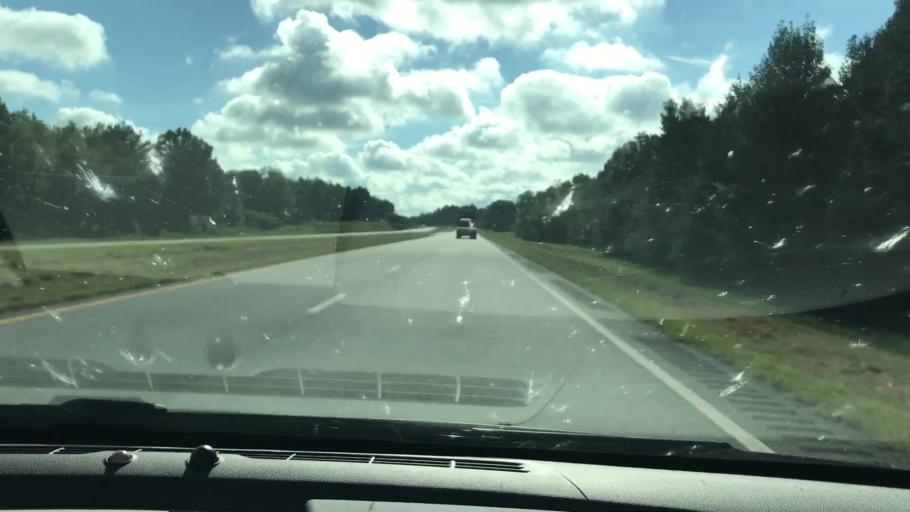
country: US
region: Georgia
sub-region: Worth County
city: Sylvester
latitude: 31.5516
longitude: -83.9743
